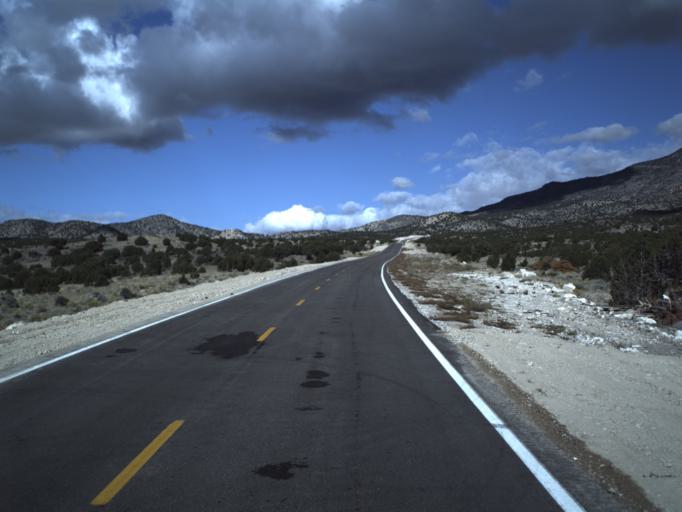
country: US
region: Utah
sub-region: Beaver County
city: Milford
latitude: 38.5034
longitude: -113.5080
